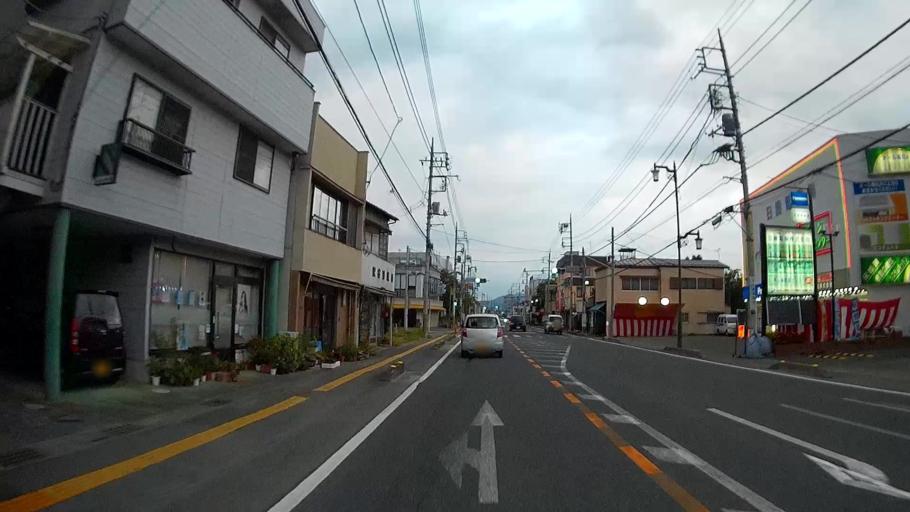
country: JP
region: Saitama
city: Chichibu
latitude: 35.9903
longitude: 139.0857
